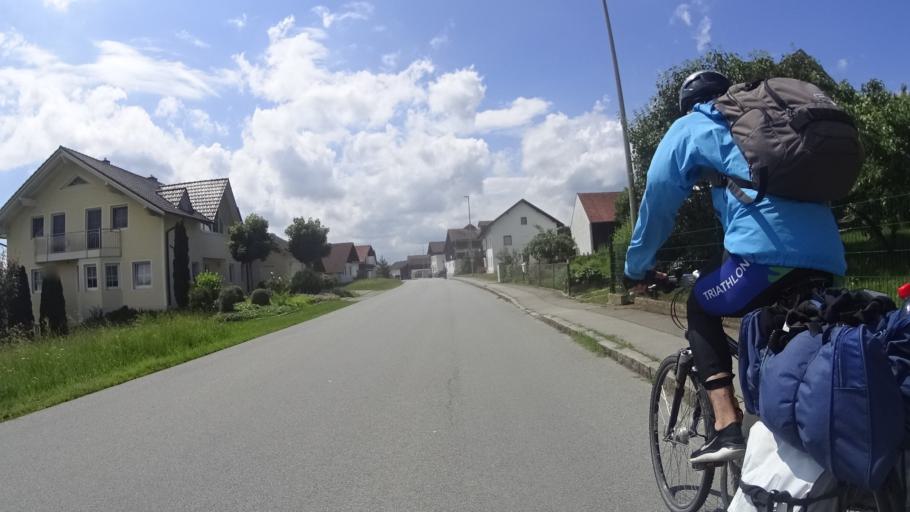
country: DE
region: Bavaria
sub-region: Lower Bavaria
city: Unterdietfurt
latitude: 48.3946
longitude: 12.6701
